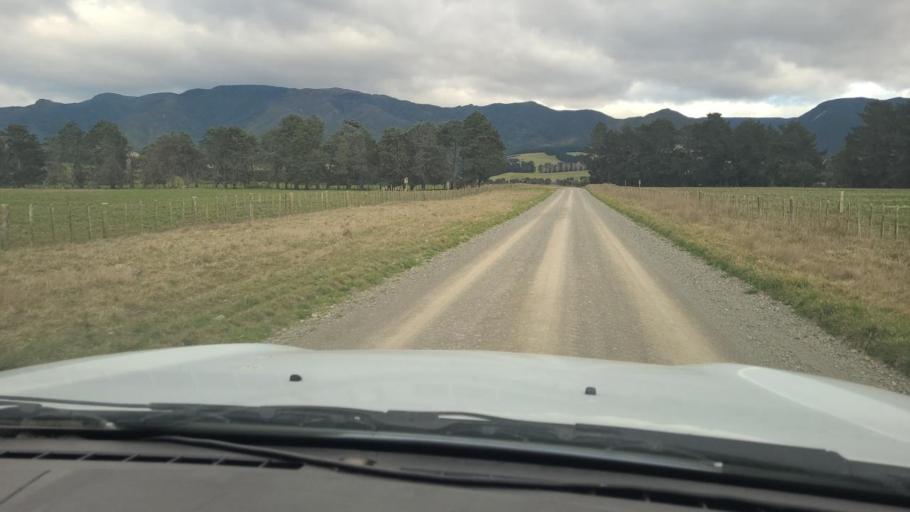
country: NZ
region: Hawke's Bay
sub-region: Hastings District
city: Hastings
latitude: -39.6066
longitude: 176.3666
